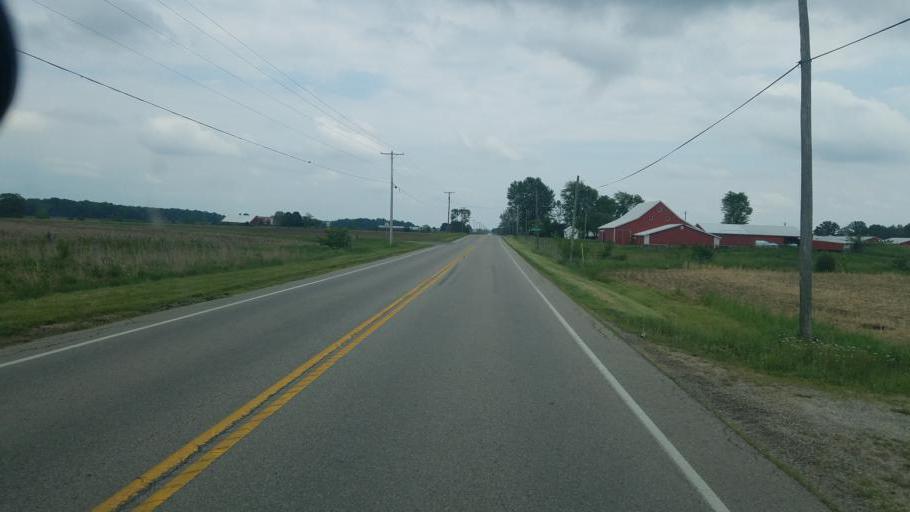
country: US
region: Ohio
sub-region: Union County
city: New California
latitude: 40.1964
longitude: -83.2980
